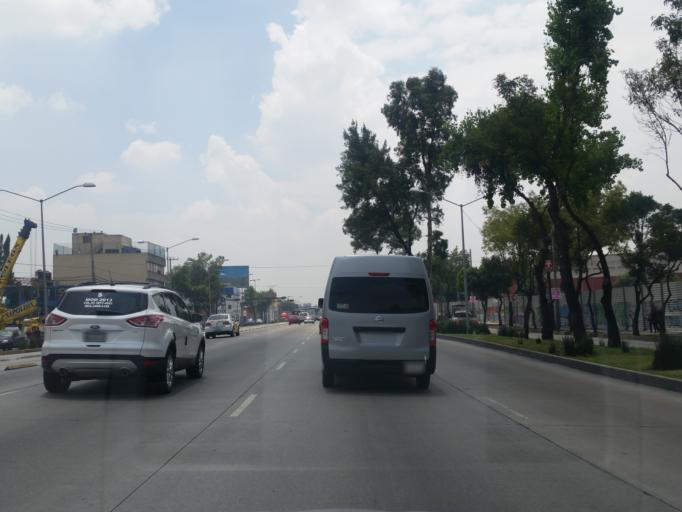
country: MX
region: Mexico
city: Colonia Lindavista
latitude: 19.4870
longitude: -99.1511
